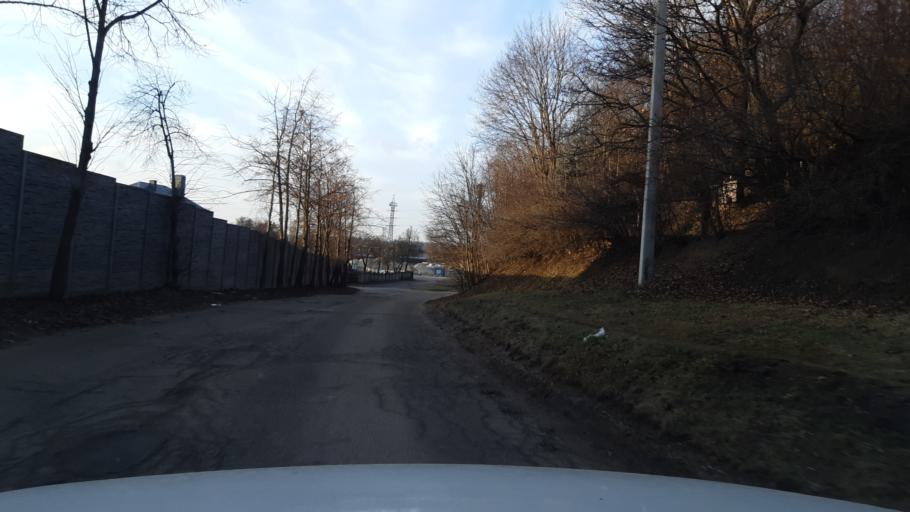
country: LT
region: Kauno apskritis
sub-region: Kaunas
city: Aleksotas
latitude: 54.8778
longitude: 23.9374
